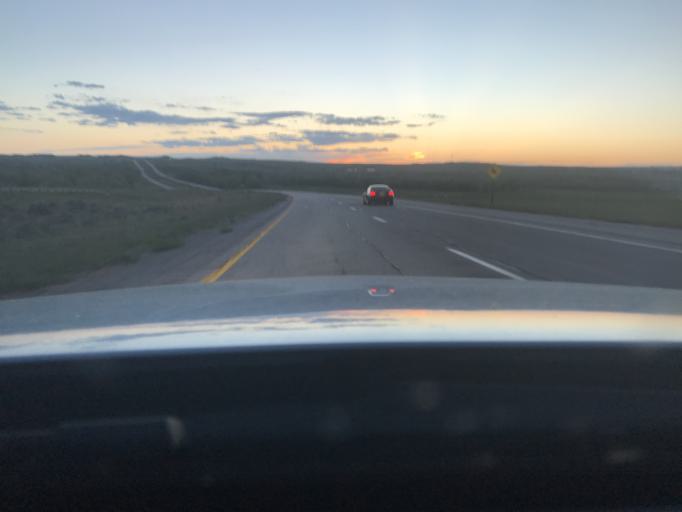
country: US
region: Wyoming
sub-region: Converse County
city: Glenrock
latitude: 42.8366
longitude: -105.8563
